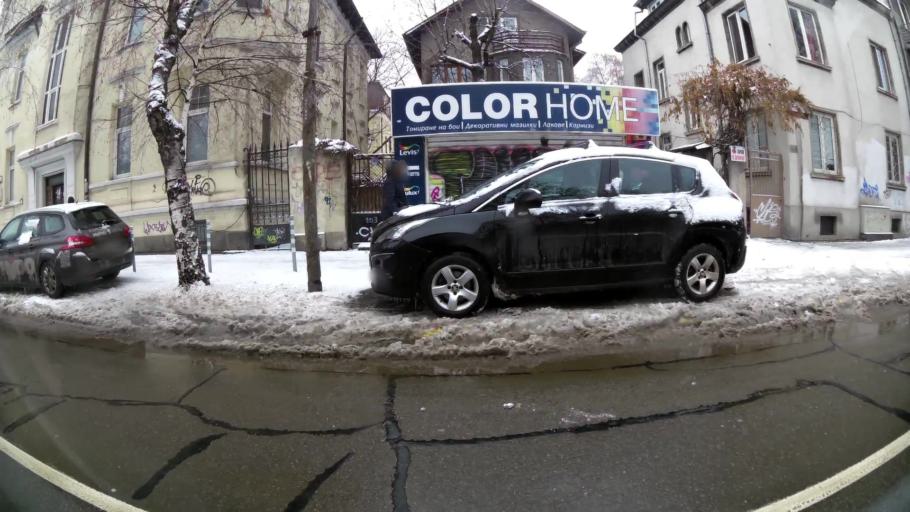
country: BG
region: Sofia-Capital
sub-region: Stolichna Obshtina
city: Sofia
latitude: 42.6944
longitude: 23.3463
